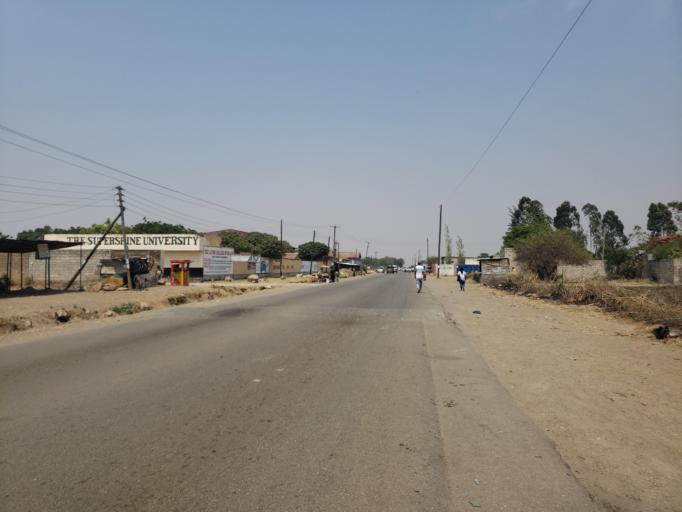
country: ZM
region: Lusaka
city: Lusaka
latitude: -15.4476
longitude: 28.2418
